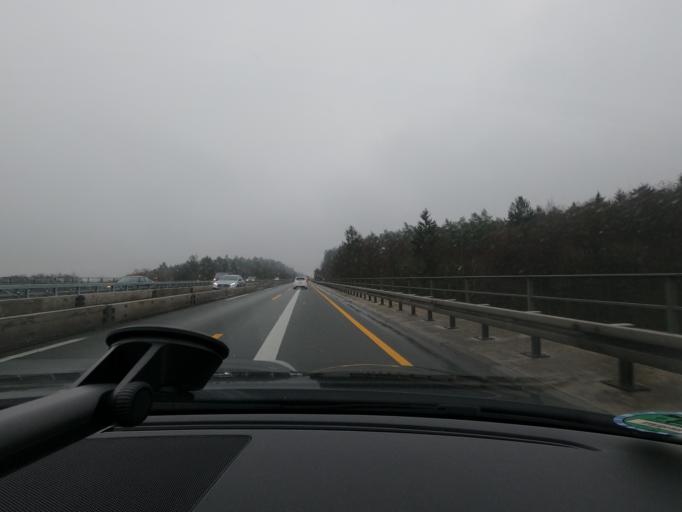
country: DE
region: Bavaria
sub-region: Upper Franconia
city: Strullendorf
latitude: 49.8546
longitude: 10.9808
